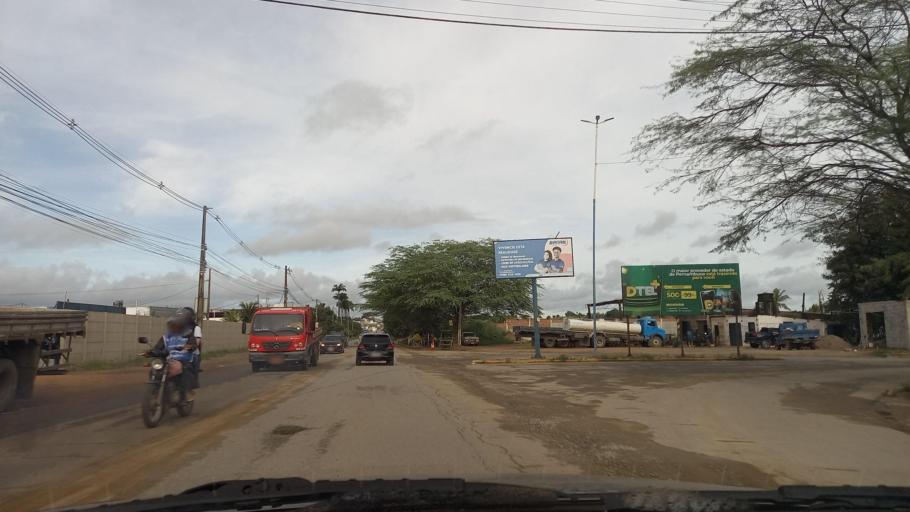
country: BR
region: Pernambuco
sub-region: Vitoria De Santo Antao
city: Vitoria de Santo Antao
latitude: -8.1188
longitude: -35.3181
